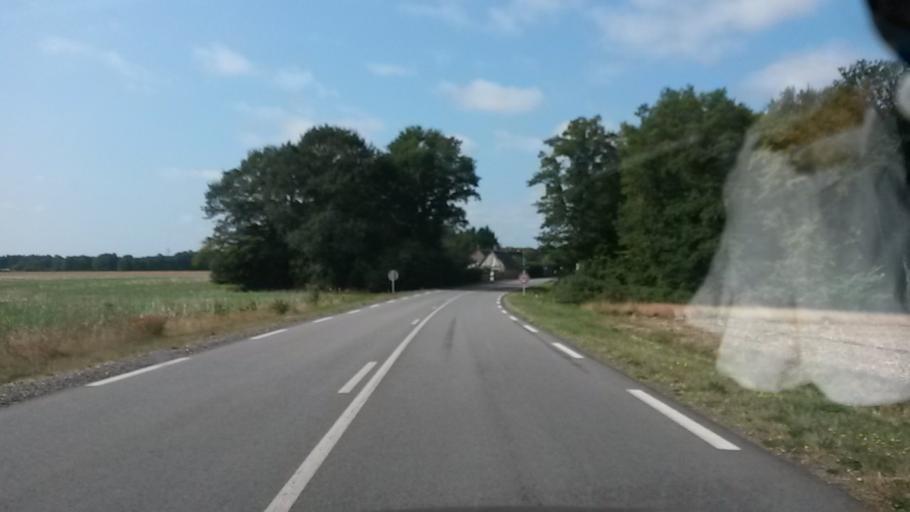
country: FR
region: Haute-Normandie
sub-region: Departement de l'Eure
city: Damville
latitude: 48.8499
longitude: 1.0556
